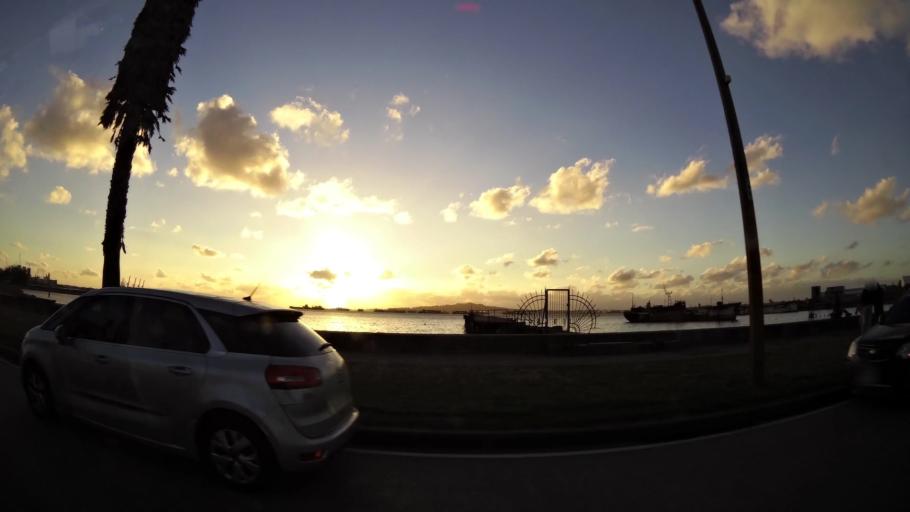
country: UY
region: Montevideo
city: Montevideo
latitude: -34.8852
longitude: -56.1984
